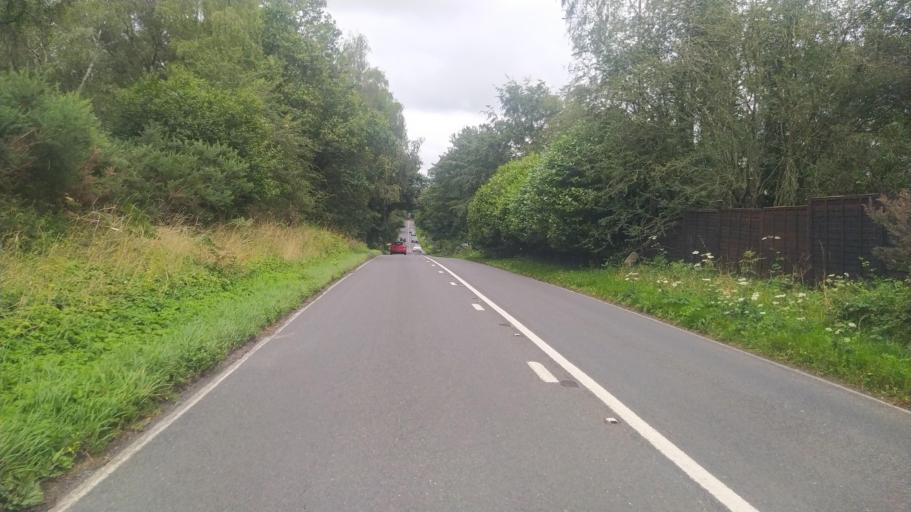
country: GB
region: England
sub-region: Hampshire
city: Liphook
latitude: 51.0603
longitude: -0.8131
